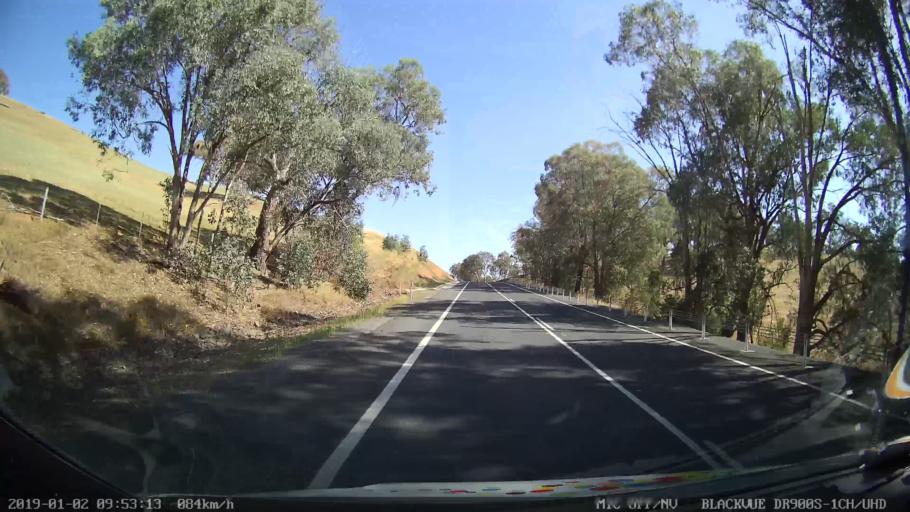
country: AU
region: New South Wales
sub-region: Tumut Shire
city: Tumut
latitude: -35.2506
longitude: 148.2035
